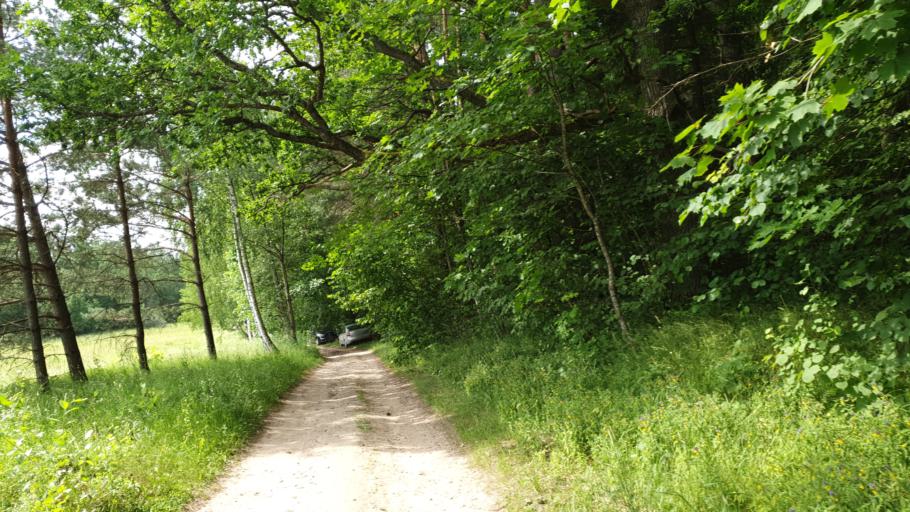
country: LT
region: Vilnius County
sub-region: Vilnius
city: Fabijoniskes
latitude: 54.7877
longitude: 25.3189
